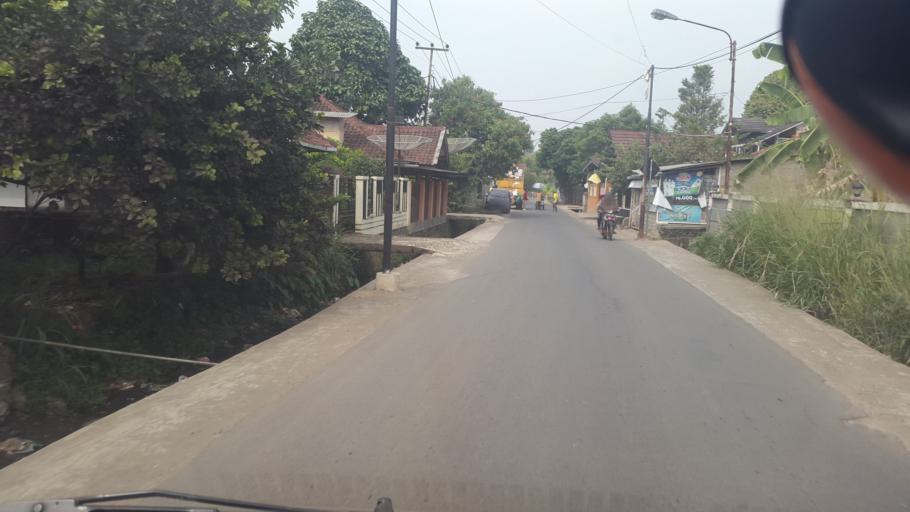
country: ID
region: West Java
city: Sukabumi
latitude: -6.9191
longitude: 106.8830
